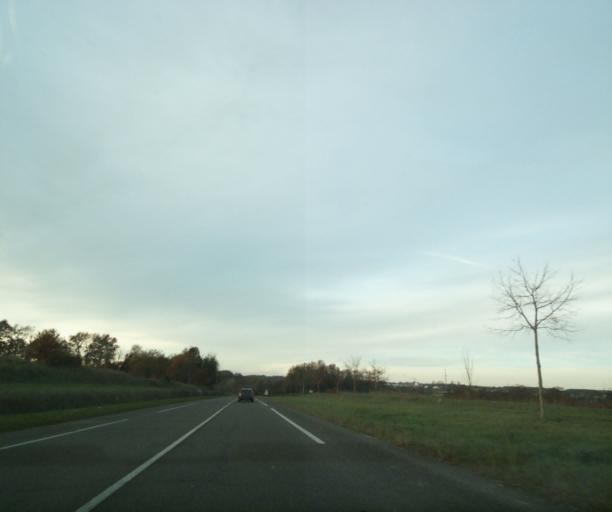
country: FR
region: Aquitaine
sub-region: Departement de la Gironde
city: Bazas
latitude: 44.4255
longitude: -0.2281
